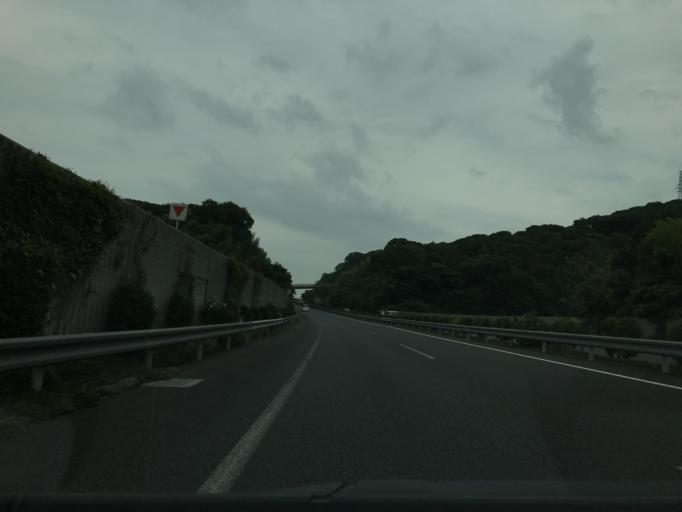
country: JP
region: Fukuoka
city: Kanda
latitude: 33.8000
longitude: 130.9532
